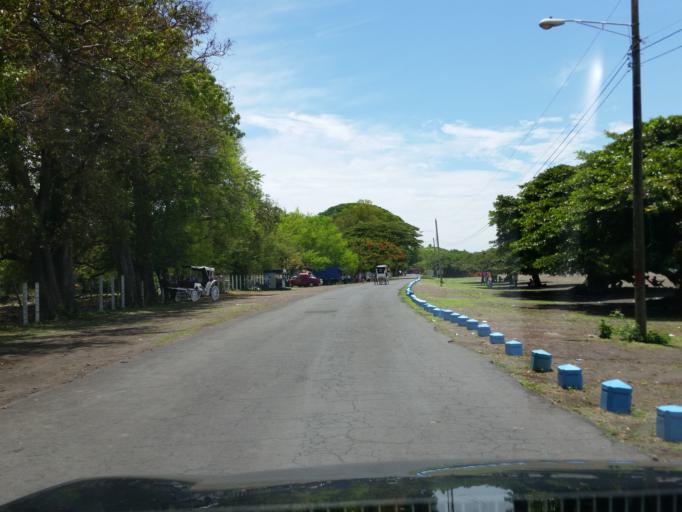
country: NI
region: Granada
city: Granada
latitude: 11.9155
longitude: -85.9350
